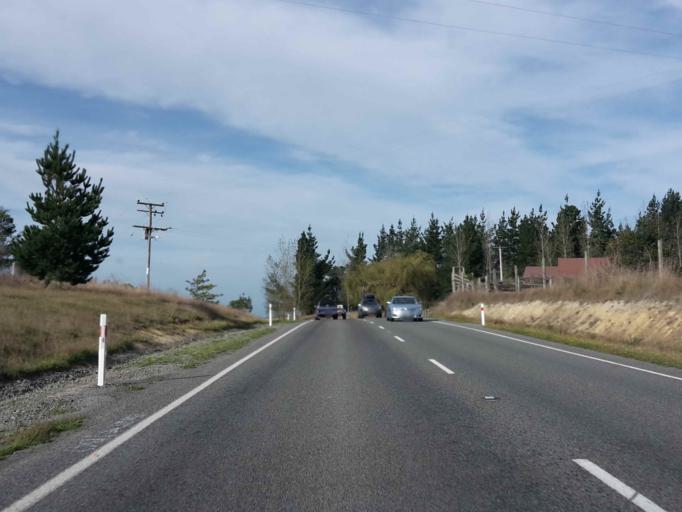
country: NZ
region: Canterbury
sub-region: Timaru District
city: Pleasant Point
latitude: -44.1230
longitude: 171.1069
